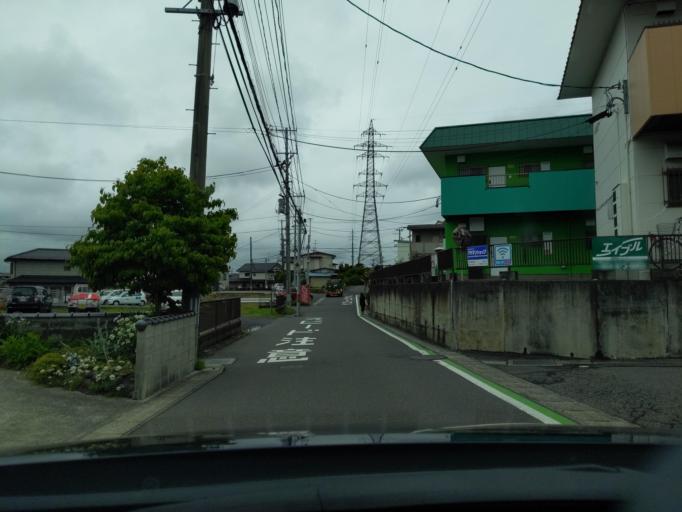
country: JP
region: Fukushima
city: Koriyama
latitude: 37.4187
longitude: 140.3777
